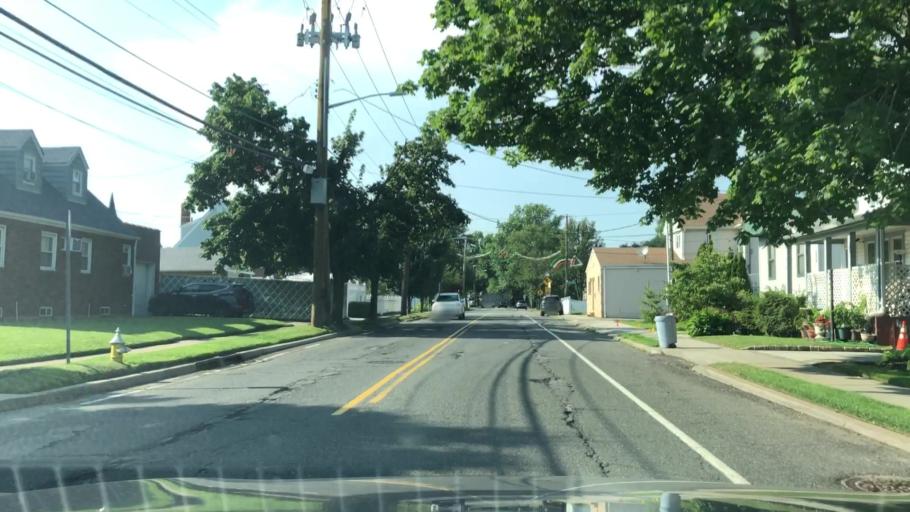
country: US
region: New York
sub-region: Nassau County
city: Franklin Square
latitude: 40.7149
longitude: -73.6775
